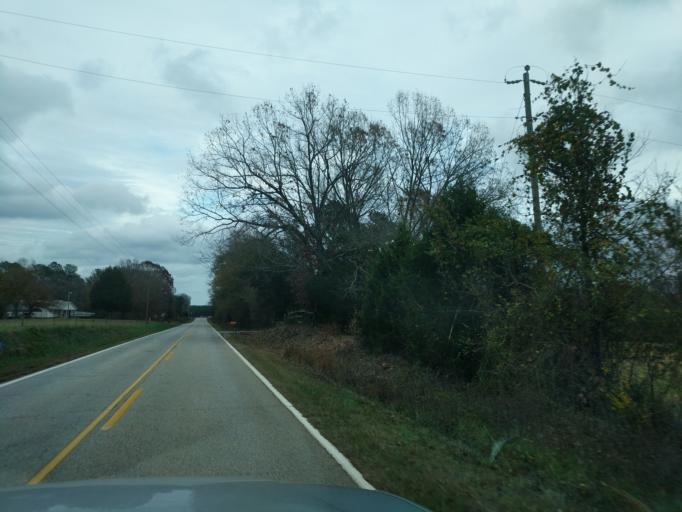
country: US
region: South Carolina
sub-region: Greenwood County
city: Ware Shoals
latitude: 34.4077
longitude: -82.1258
